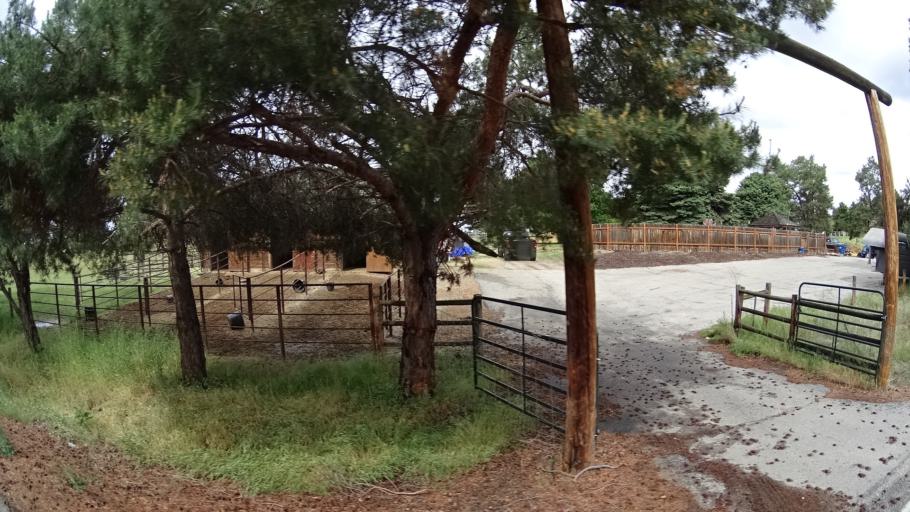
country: US
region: Idaho
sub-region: Ada County
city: Eagle
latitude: 43.7364
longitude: -116.3573
